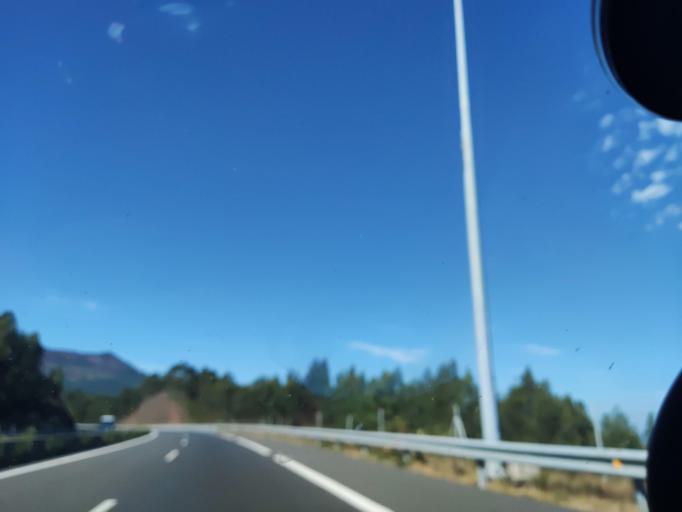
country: ES
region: Galicia
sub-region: Provincia da Coruna
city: Boiro
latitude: 42.5884
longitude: -8.9751
